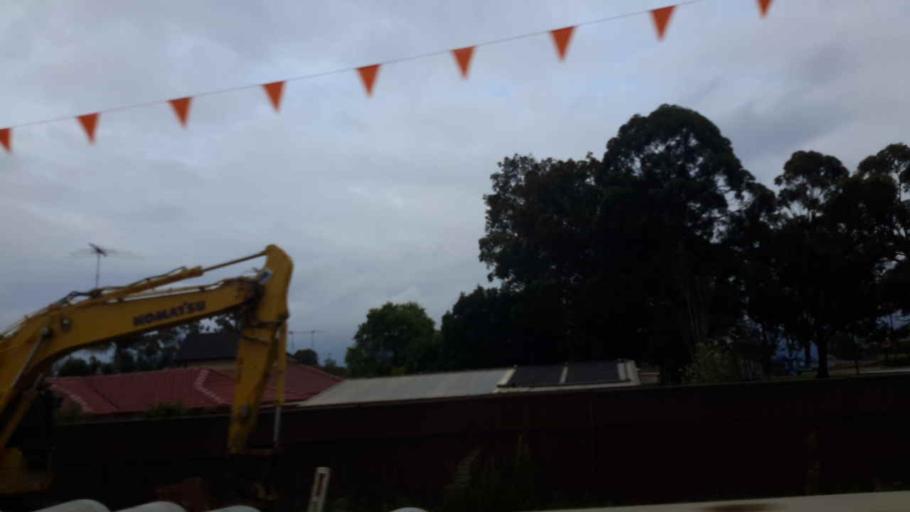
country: AU
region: New South Wales
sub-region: Penrith Municipality
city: Kingswood Park
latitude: -33.7788
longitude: 150.7112
